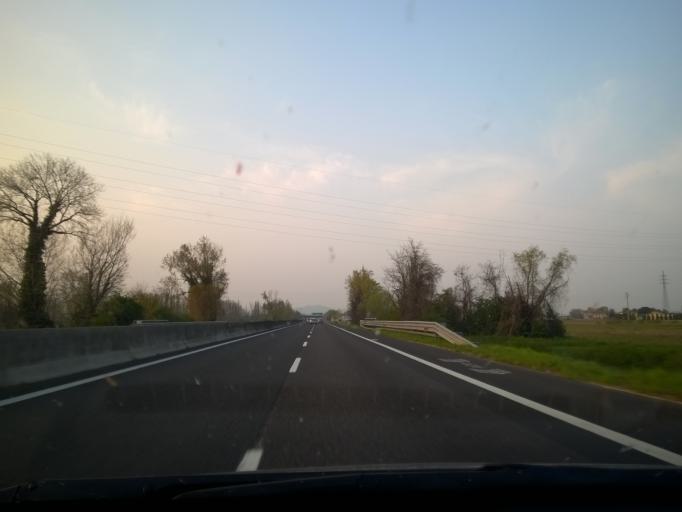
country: IT
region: Veneto
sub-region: Provincia di Padova
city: Monselice
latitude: 45.2283
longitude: 11.7747
